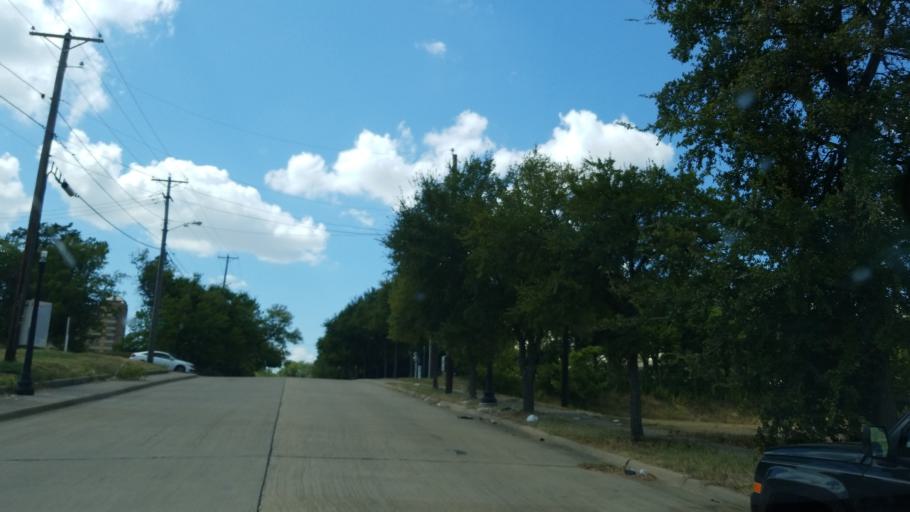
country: US
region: Texas
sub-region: Dallas County
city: Dallas
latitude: 32.7624
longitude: -96.8210
